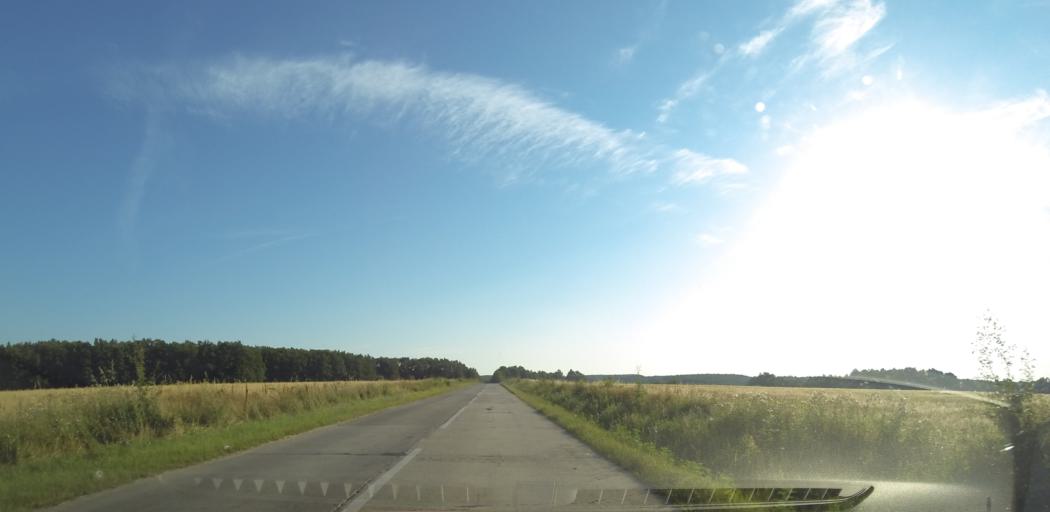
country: RO
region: Valcea
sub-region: Comuna Balcesti
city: Balcesti
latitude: 44.5879
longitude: 23.9135
